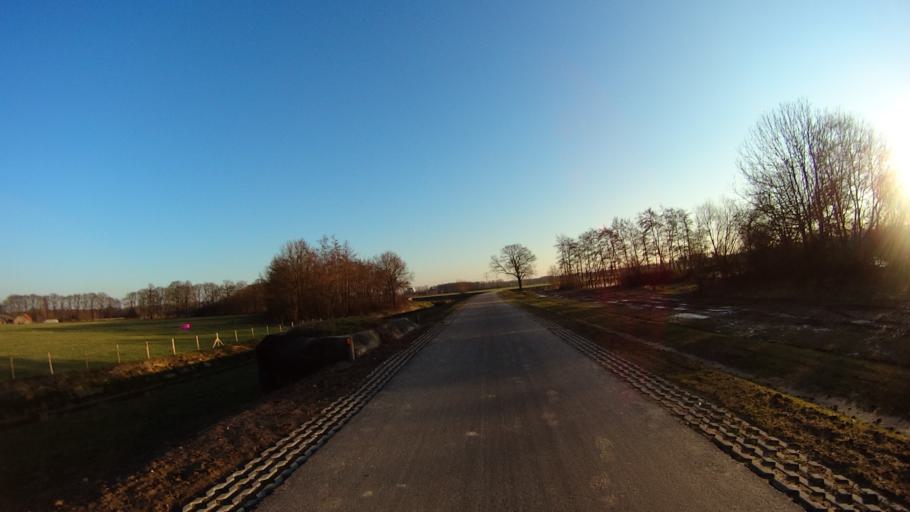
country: NL
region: Utrecht
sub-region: Gemeente Amersfoort
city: Hoogland
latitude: 52.1791
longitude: 5.3410
